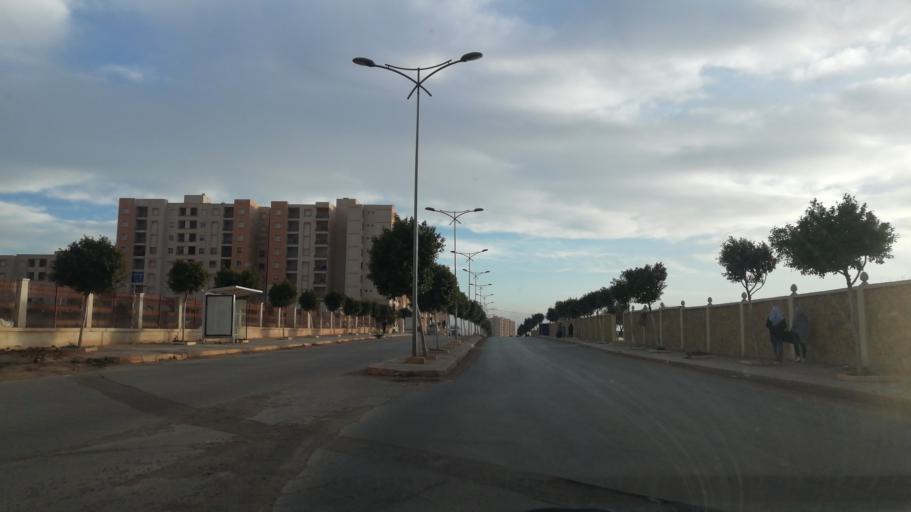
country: DZ
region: Oran
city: Bir el Djir
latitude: 35.6939
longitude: -0.5857
